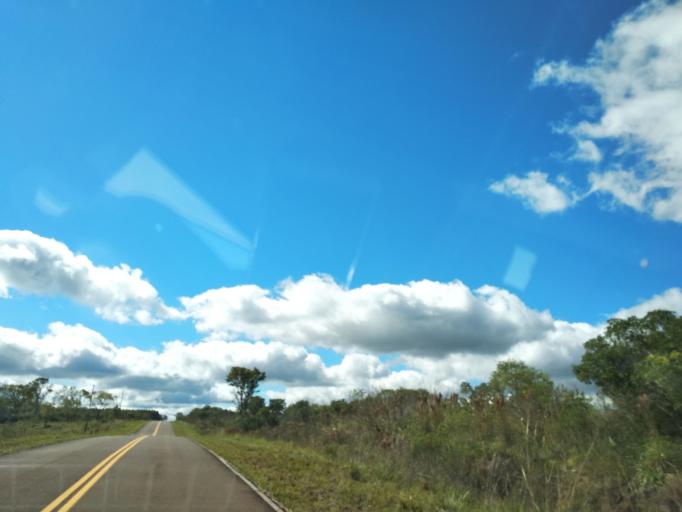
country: AR
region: Misiones
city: Santa Ana
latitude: -27.4124
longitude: -55.5598
